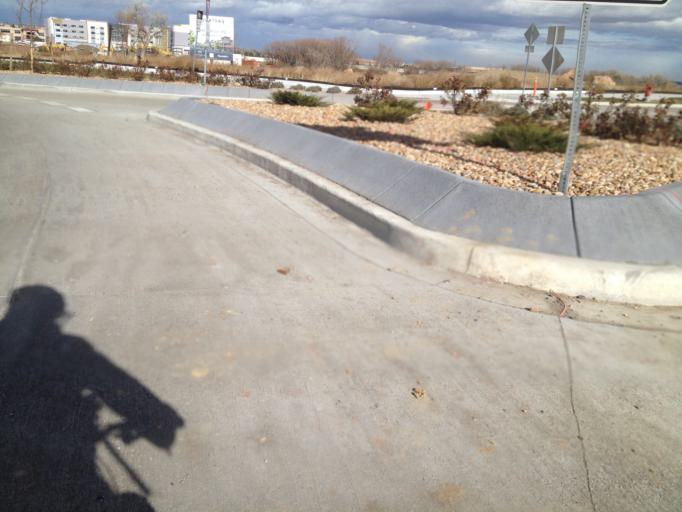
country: US
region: Colorado
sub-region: Boulder County
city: Superior
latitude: 39.9516
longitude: -105.1648
